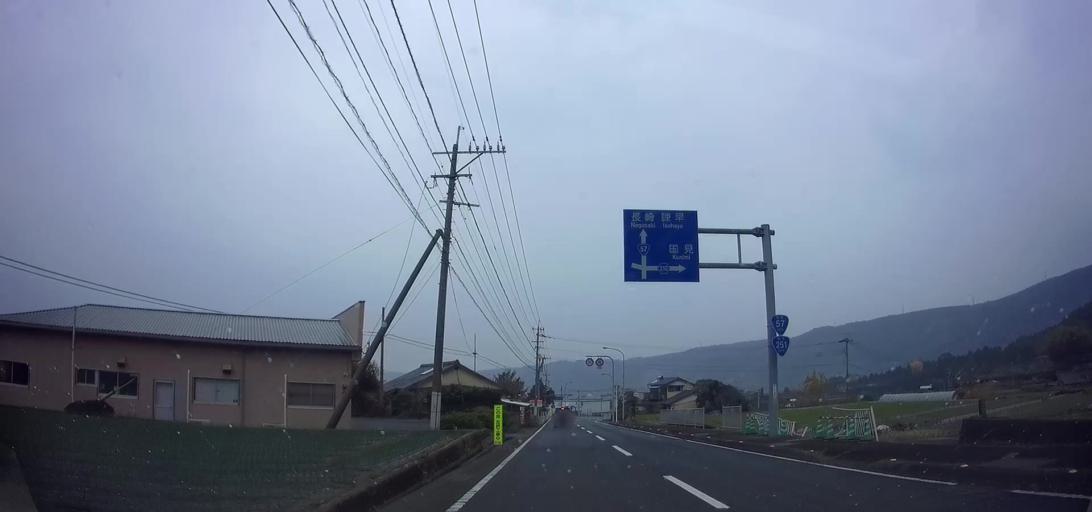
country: JP
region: Nagasaki
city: Shimabara
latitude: 32.7814
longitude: 130.2065
